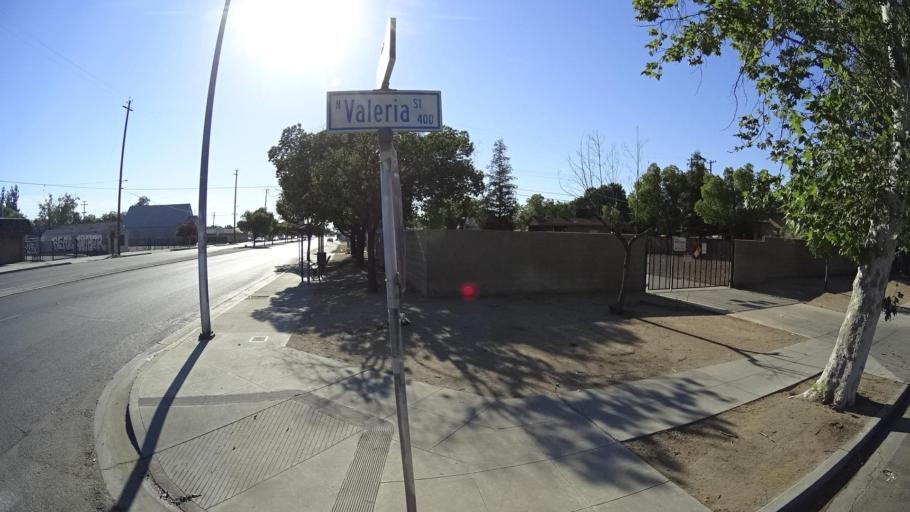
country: US
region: California
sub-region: Fresno County
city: Fresno
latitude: 36.7502
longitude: -119.7849
